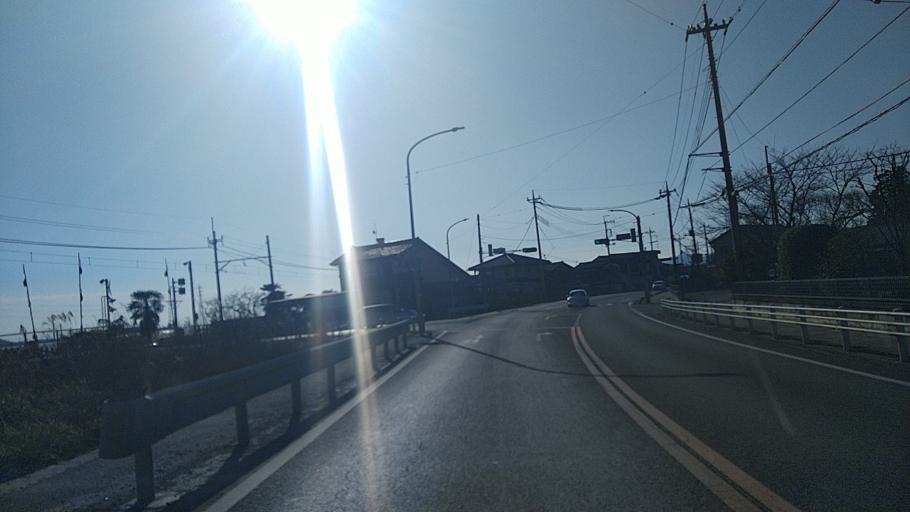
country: JP
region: Tochigi
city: Tanuma
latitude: 36.3741
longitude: 139.5898
